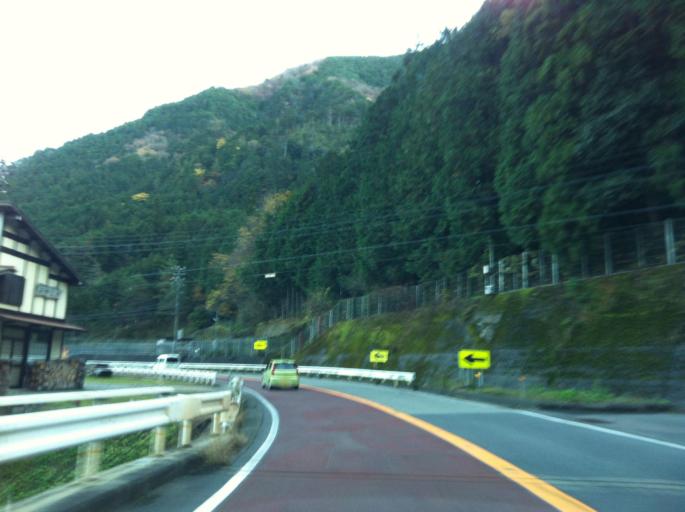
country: JP
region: Gifu
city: Minokamo
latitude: 35.5989
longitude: 137.1558
